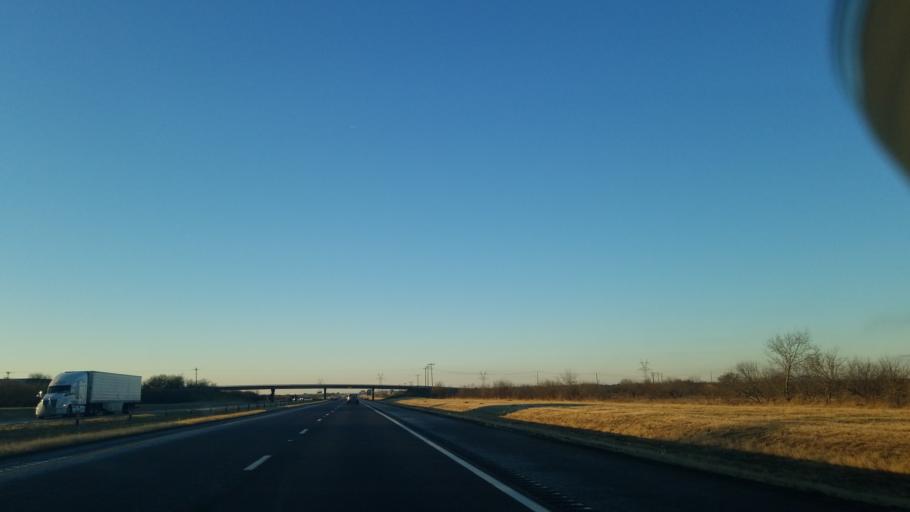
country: US
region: Texas
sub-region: Denton County
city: Argyle
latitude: 33.1212
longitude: -97.2135
